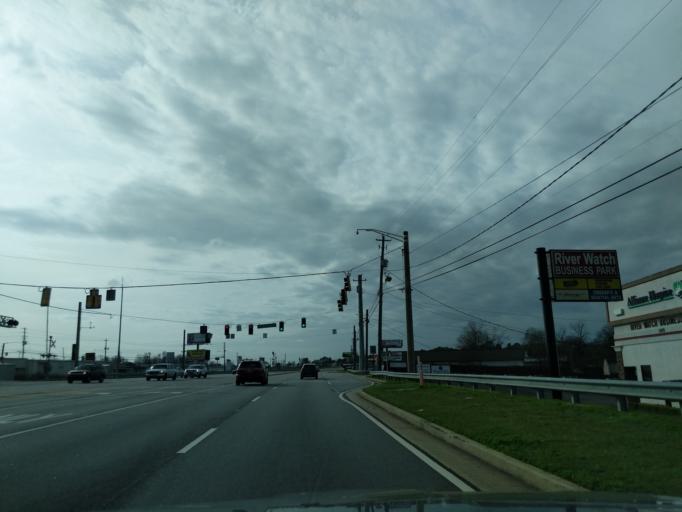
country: US
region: Georgia
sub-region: Columbia County
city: Martinez
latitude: 33.5172
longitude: -82.0699
